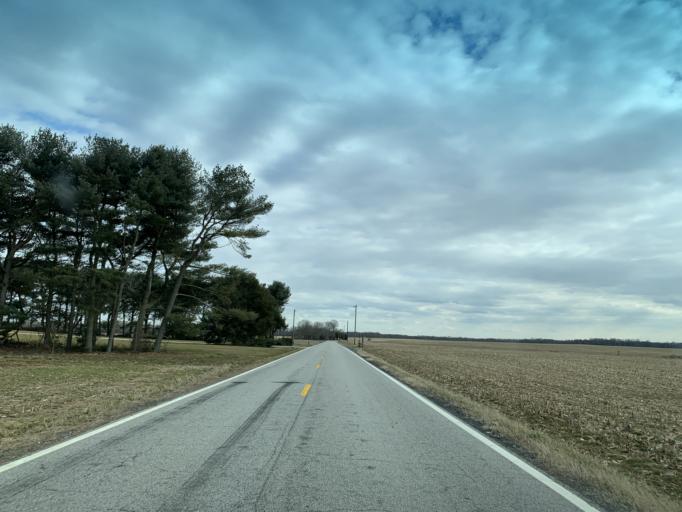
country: US
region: Maryland
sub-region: Caroline County
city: Ridgely
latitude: 38.9921
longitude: -75.9504
